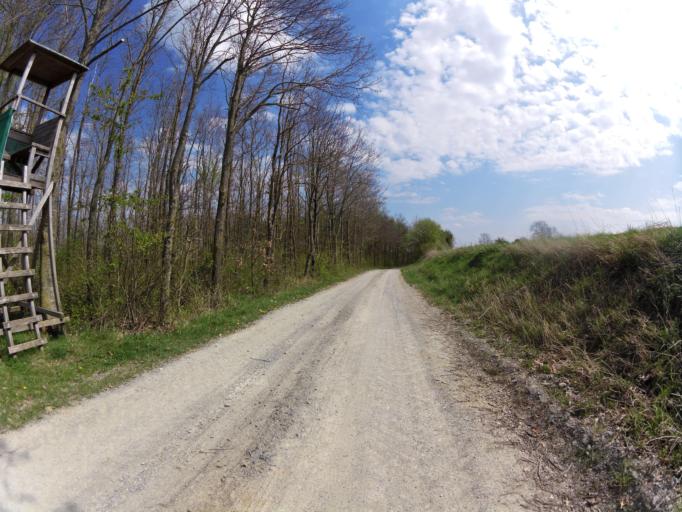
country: DE
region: Bavaria
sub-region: Regierungsbezirk Unterfranken
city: Winterhausen
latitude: 49.6861
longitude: 10.0142
